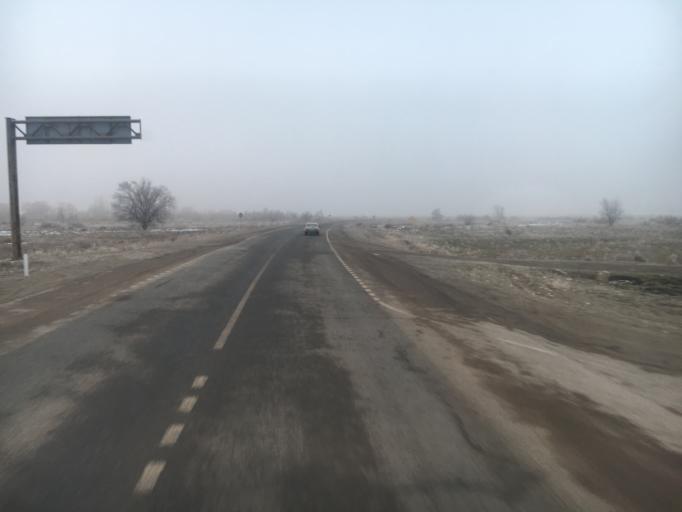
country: KZ
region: Zhambyl
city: Sarykemer
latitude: 43.0406
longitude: 71.5331
